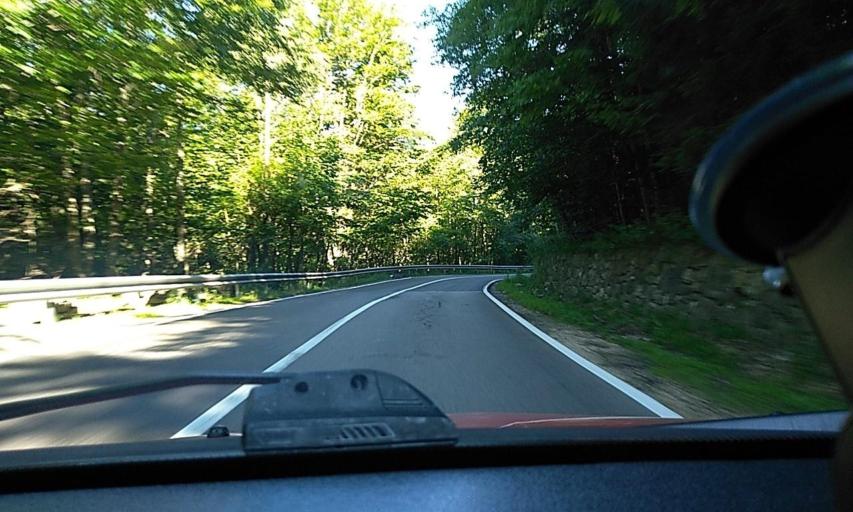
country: RO
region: Brasov
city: Crivina
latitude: 45.4966
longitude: 25.8610
